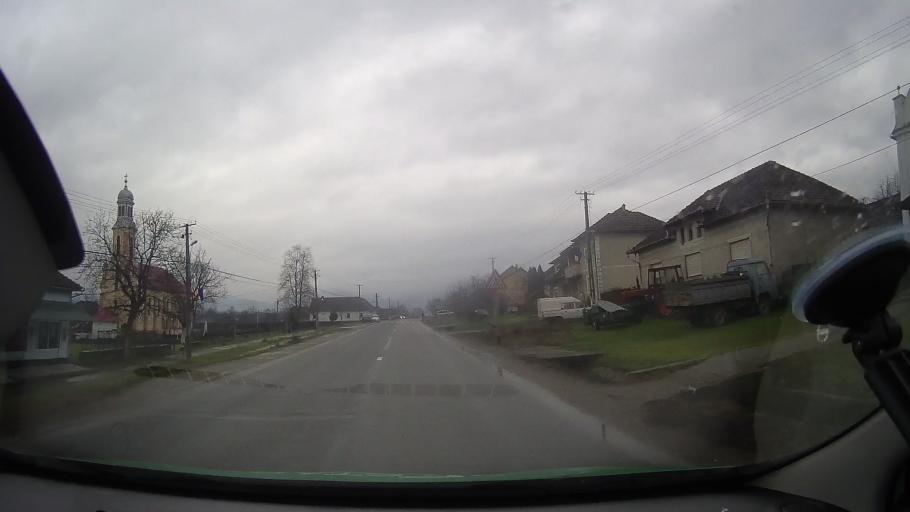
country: RO
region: Arad
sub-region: Comuna Gurahont
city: Gurahont
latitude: 46.2744
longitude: 22.3035
